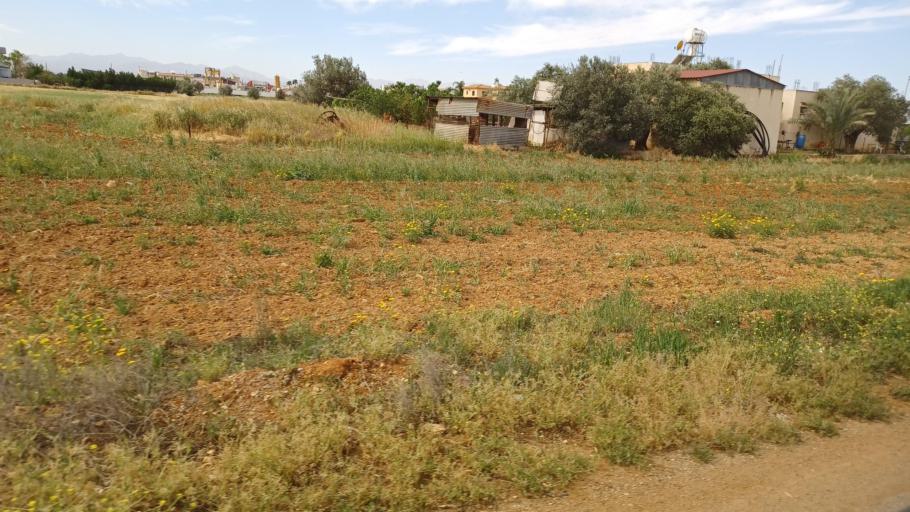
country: CY
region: Lefkosia
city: Kokkinotrimithia
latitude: 35.1519
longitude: 33.2108
